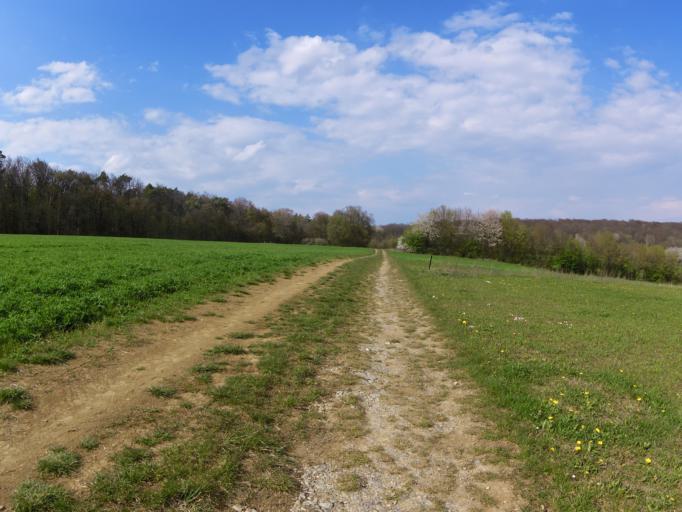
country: DE
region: Bavaria
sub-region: Regierungsbezirk Unterfranken
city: Rimpar
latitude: 49.8720
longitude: 9.9603
